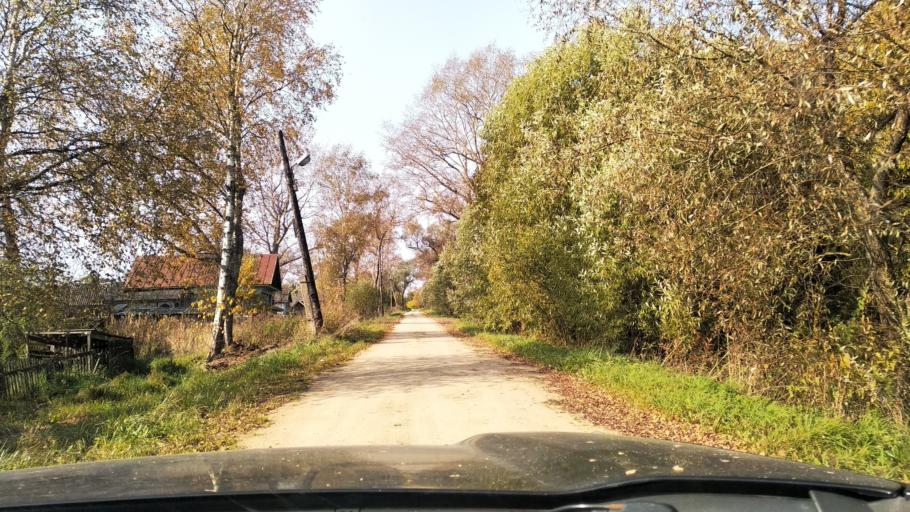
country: RU
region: Tverskaya
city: Krasnyy Kholm
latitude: 58.0331
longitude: 37.1831
